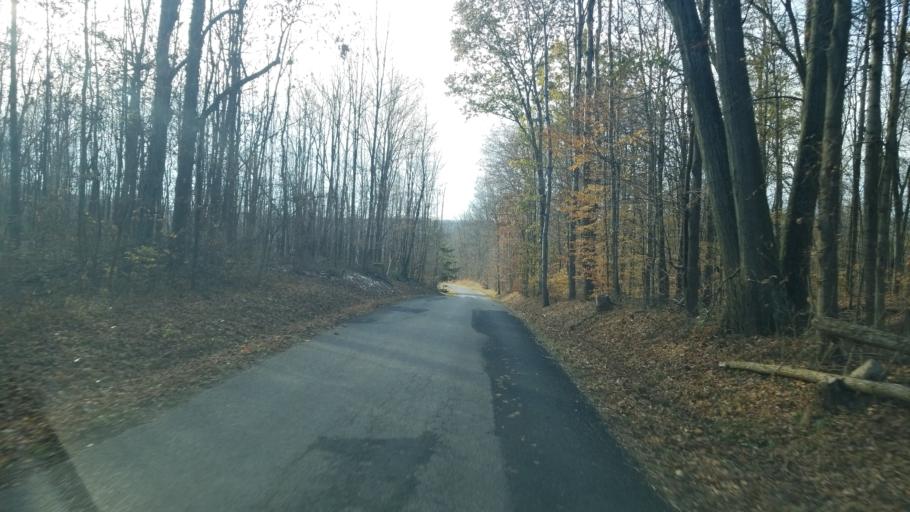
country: US
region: Ohio
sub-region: Ashland County
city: Loudonville
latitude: 40.7196
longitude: -82.3344
